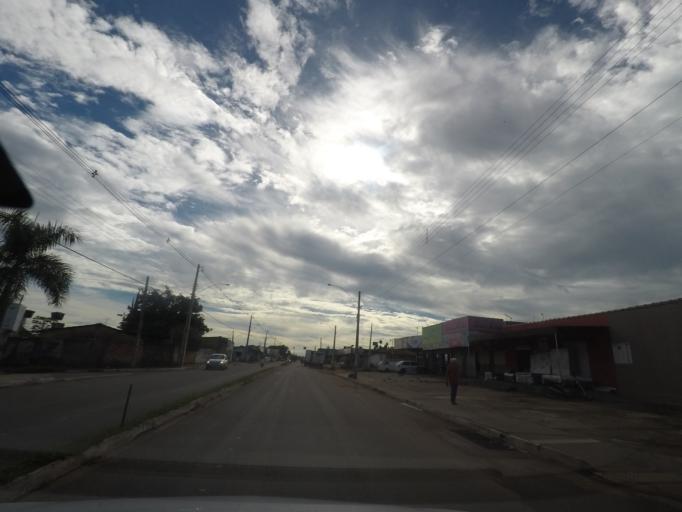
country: BR
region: Goias
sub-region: Aparecida De Goiania
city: Aparecida de Goiania
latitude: -16.8162
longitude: -49.3146
